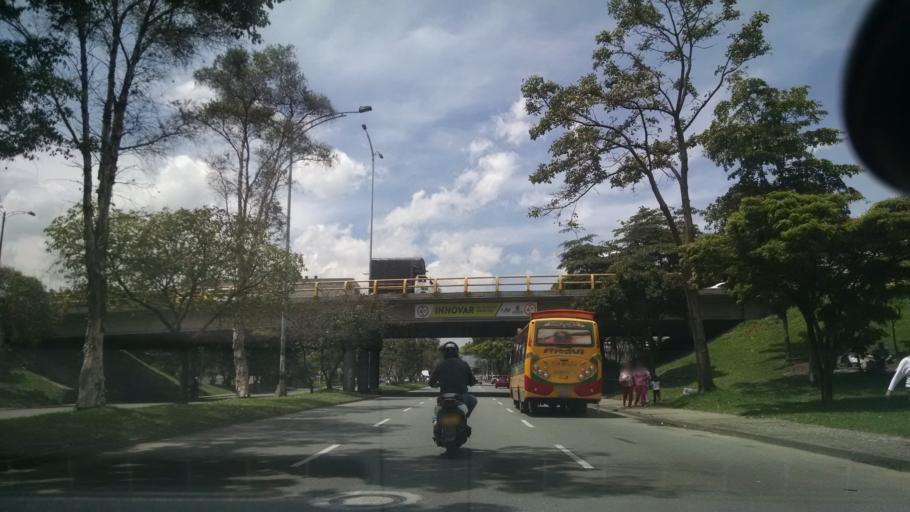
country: CO
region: Antioquia
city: Itagui
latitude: 6.2049
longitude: -75.5870
